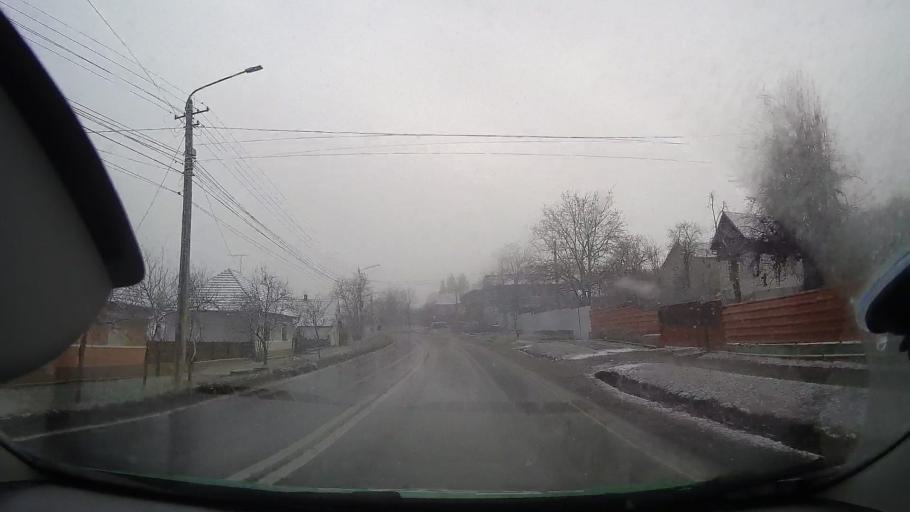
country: RO
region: Mures
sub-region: Comuna Bagaciu
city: Delenii
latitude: 46.2775
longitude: 24.3007
